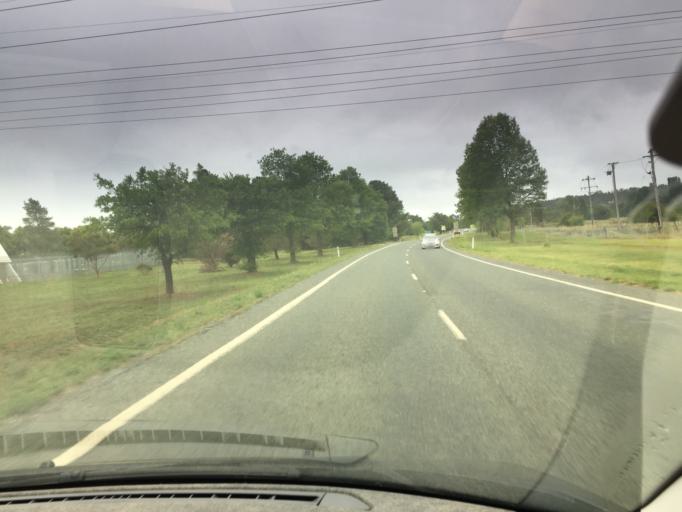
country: AU
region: New South Wales
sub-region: Cooma-Monaro
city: Cooma
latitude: -36.2173
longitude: 149.1404
